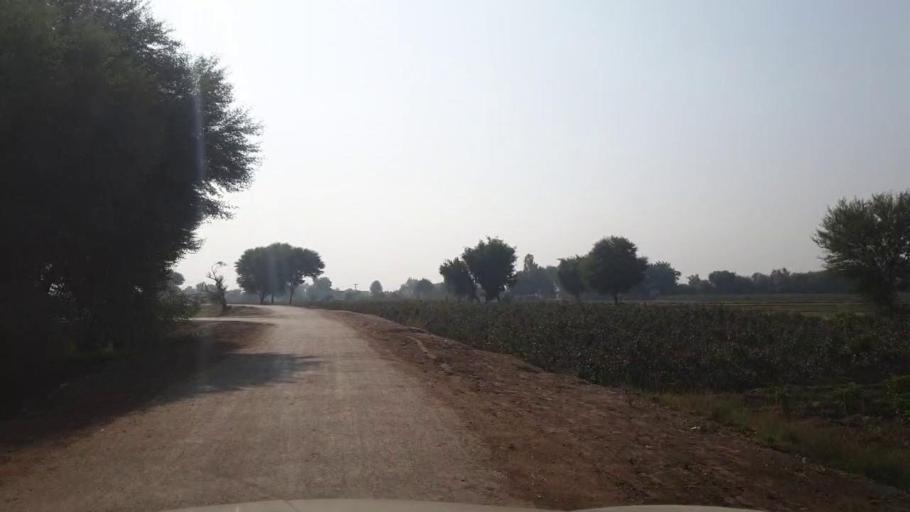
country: PK
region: Sindh
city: Bhan
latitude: 26.5041
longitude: 67.7902
